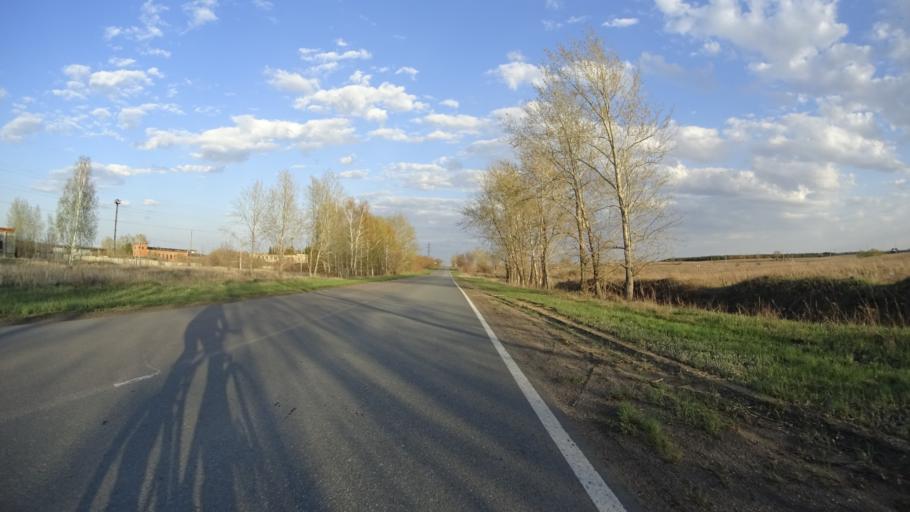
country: RU
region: Chelyabinsk
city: Troitsk
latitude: 54.0558
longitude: 61.5864
